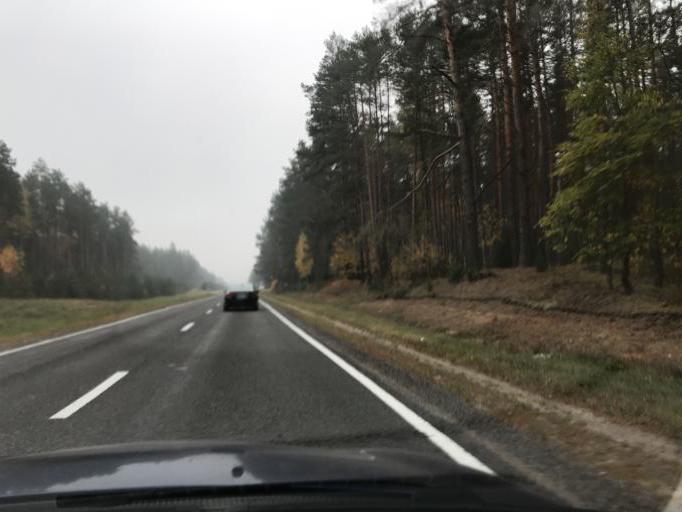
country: LT
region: Alytaus apskritis
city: Druskininkai
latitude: 53.8649
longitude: 23.8935
